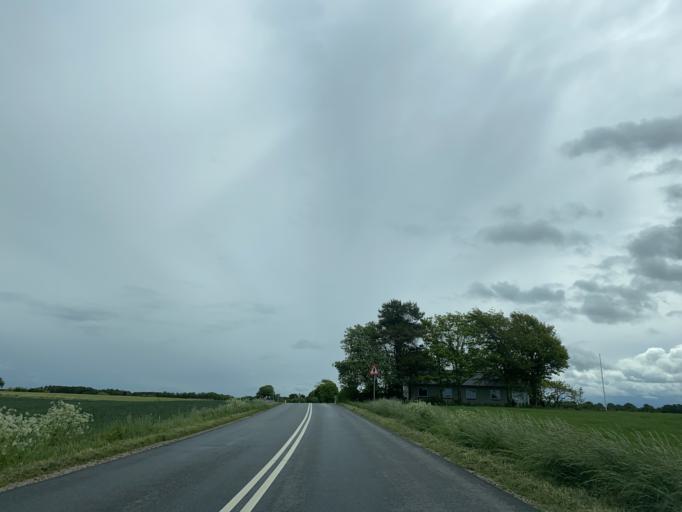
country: DK
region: Central Jutland
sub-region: Arhus Kommune
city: Sabro
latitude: 56.2498
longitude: 9.9948
